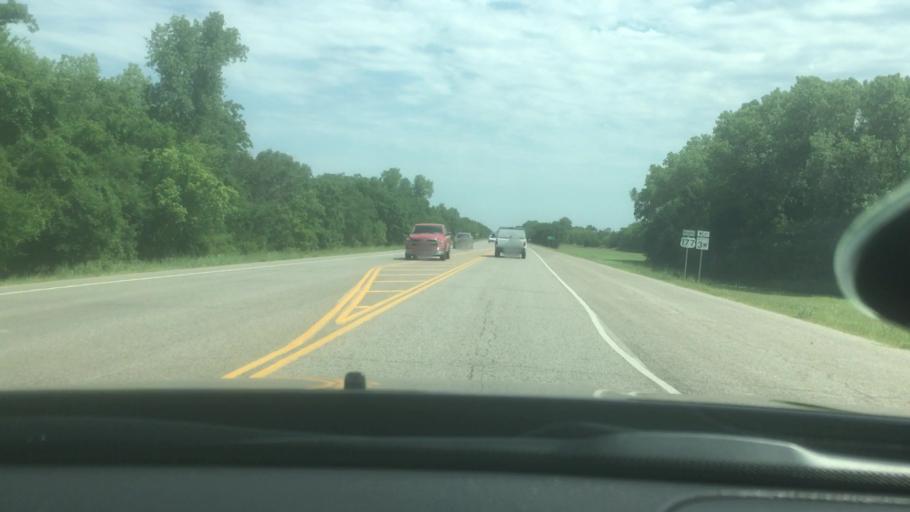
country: US
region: Oklahoma
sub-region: Seminole County
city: Maud
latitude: 35.0732
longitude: -96.9312
